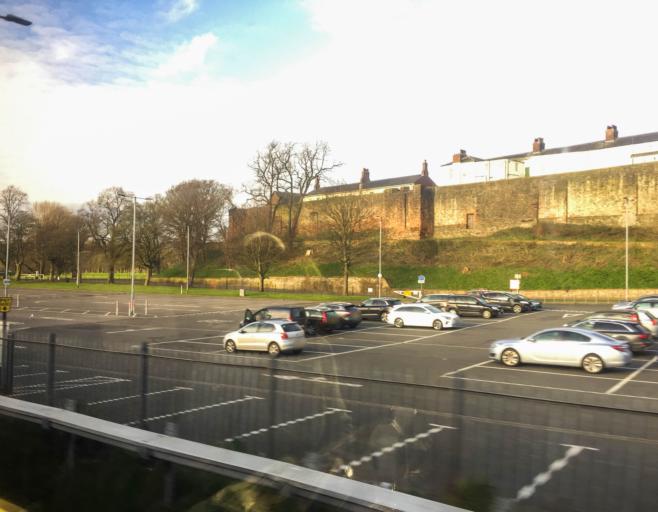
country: GB
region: England
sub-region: Cumbria
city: Carlisle
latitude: 54.8966
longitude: -2.9442
